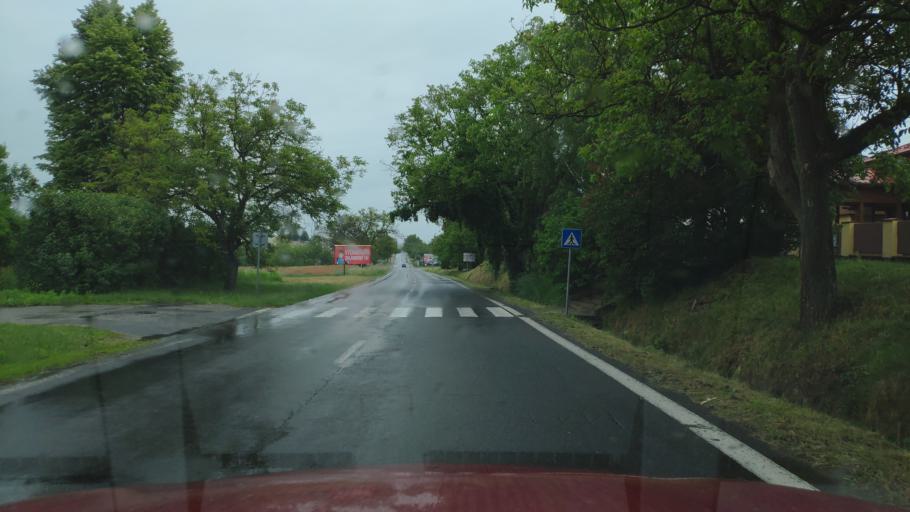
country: HU
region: Borsod-Abauj-Zemplen
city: Ricse
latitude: 48.4321
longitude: 21.9696
